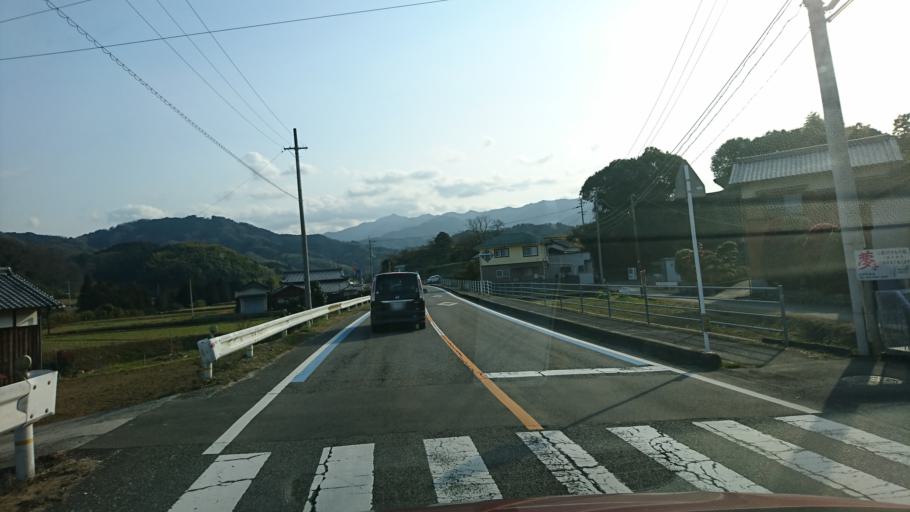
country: JP
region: Ehime
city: Hojo
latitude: 34.0071
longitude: 132.9383
